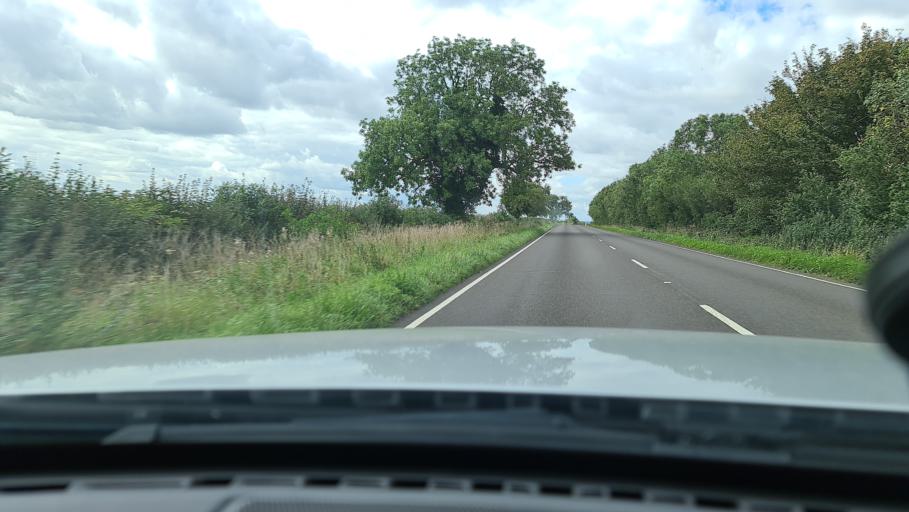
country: GB
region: England
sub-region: Oxfordshire
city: Somerton
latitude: 51.9717
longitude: -1.2270
